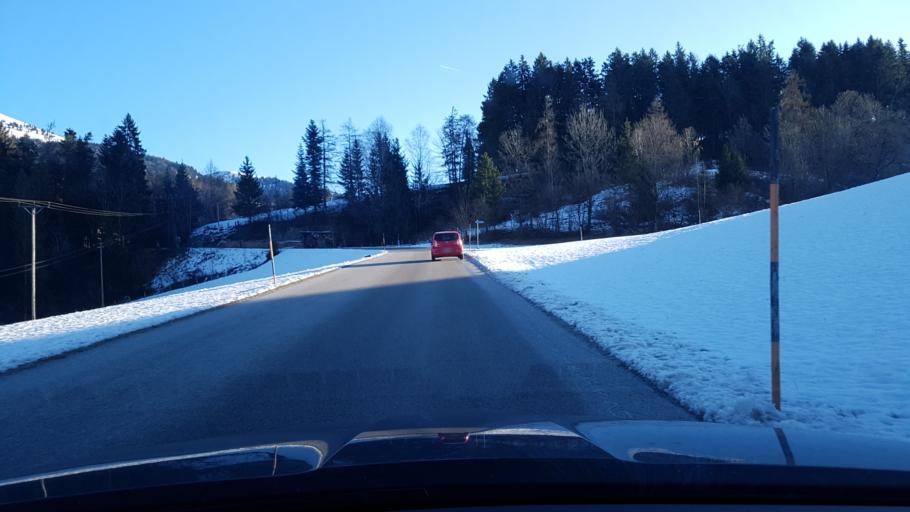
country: AT
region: Salzburg
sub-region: Politischer Bezirk Hallein
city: Kuchl
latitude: 47.6586
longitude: 13.1805
